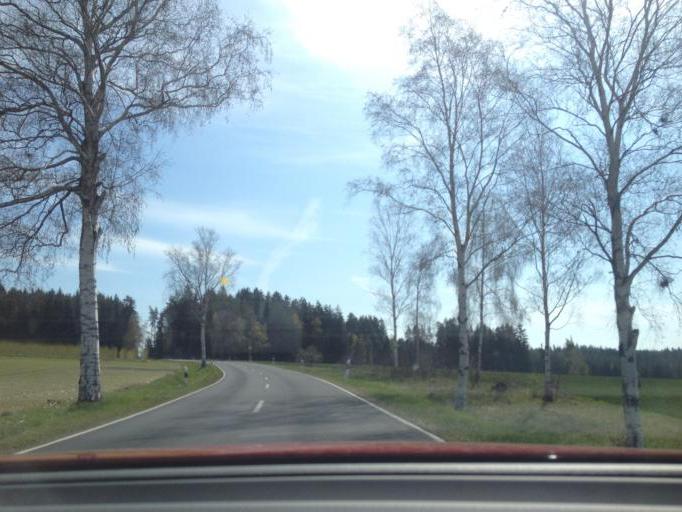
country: DE
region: Bavaria
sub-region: Upper Franconia
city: Roslau
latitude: 50.0762
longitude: 12.0205
